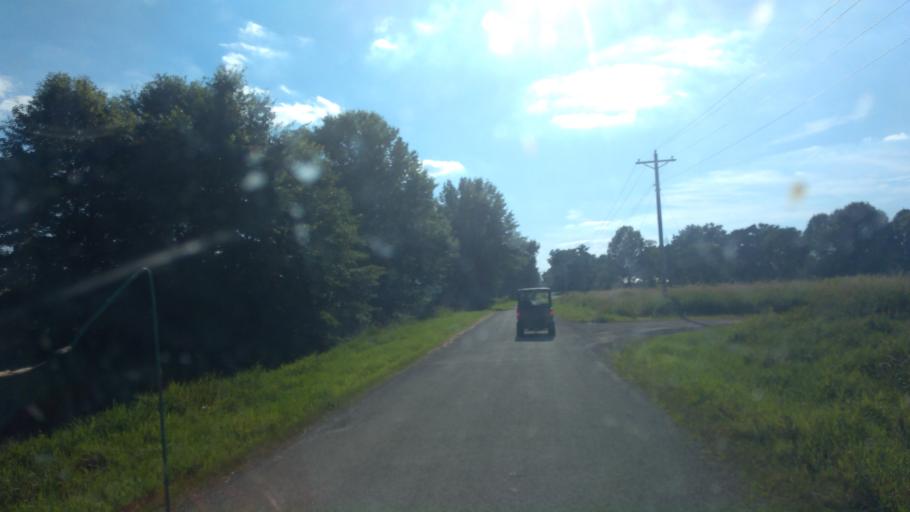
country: US
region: Ohio
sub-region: Wayne County
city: Shreve
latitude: 40.7340
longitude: -82.0738
